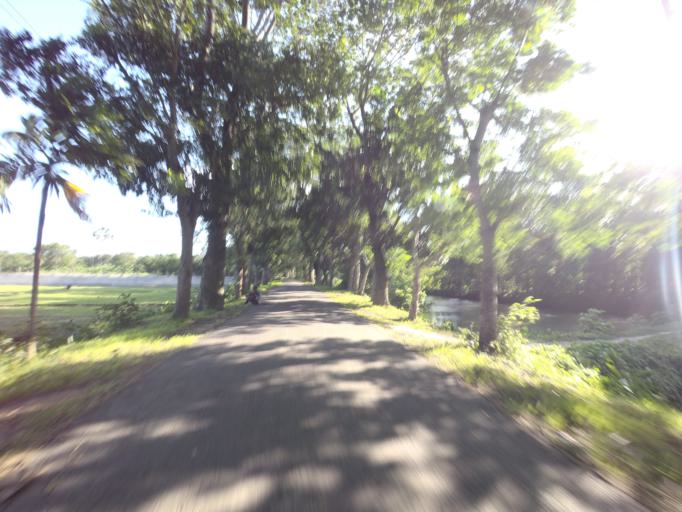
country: BD
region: Khulna
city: Kalia
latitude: 22.9550
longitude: 89.5511
